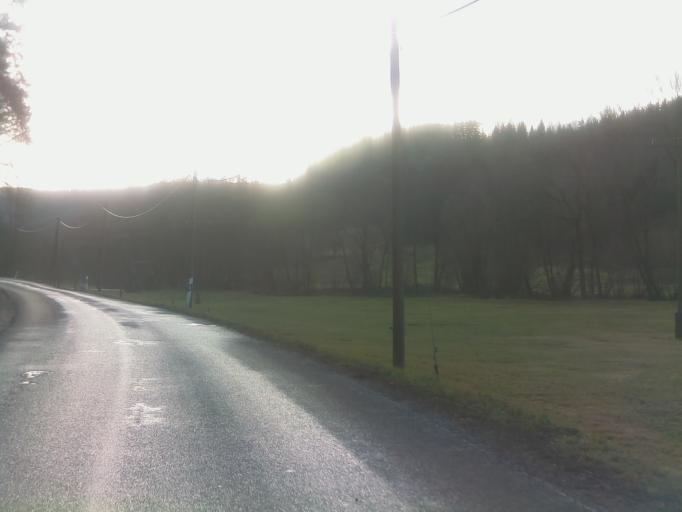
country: DE
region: Thuringia
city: Rottenbach
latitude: 50.7036
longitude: 11.1993
